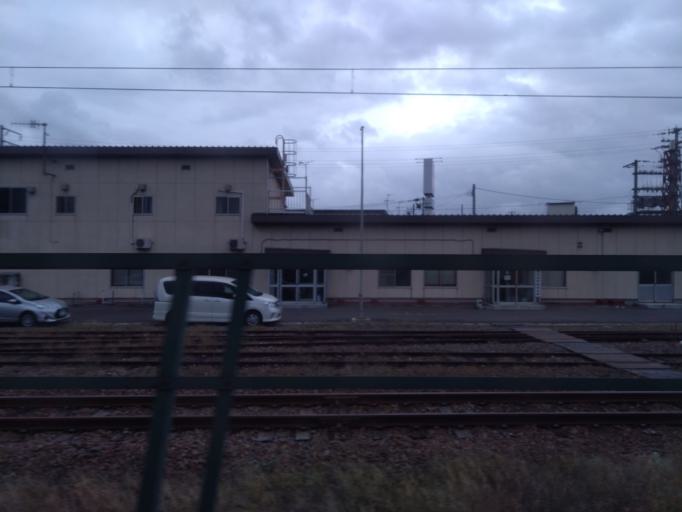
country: JP
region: Hokkaido
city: Hakodate
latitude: 41.8043
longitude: 140.7335
